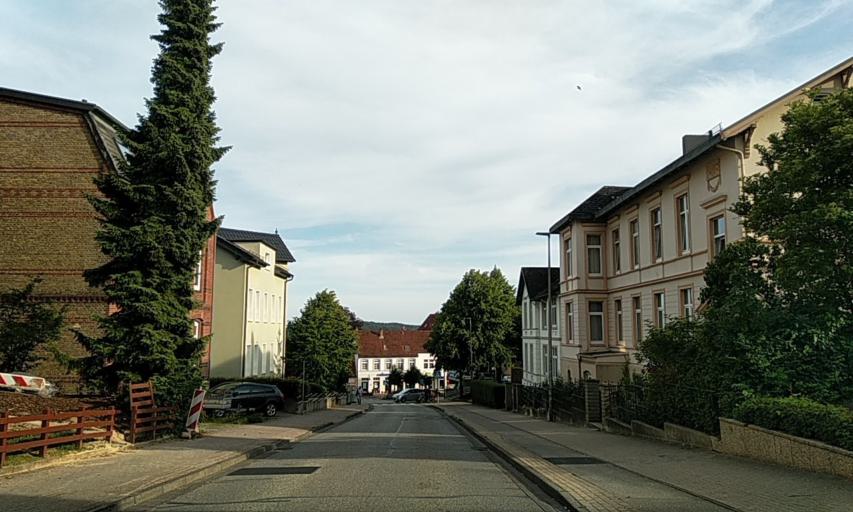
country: DE
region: Schleswig-Holstein
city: Schleswig
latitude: 54.5169
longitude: 9.5586
